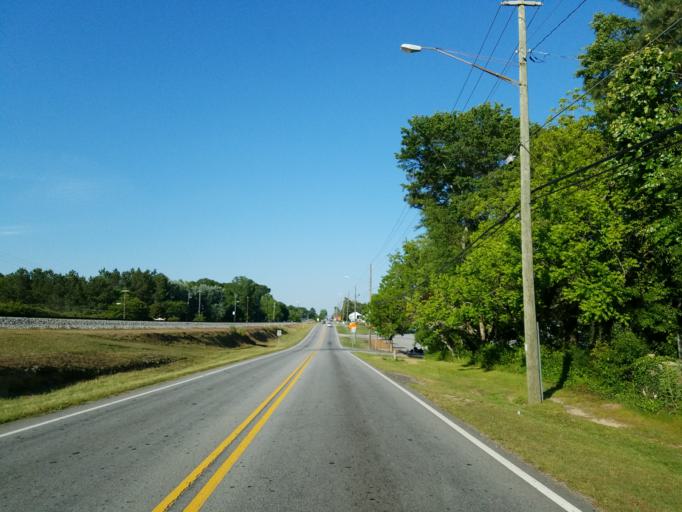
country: US
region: Georgia
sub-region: Douglas County
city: Douglasville
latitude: 33.7461
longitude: -84.7614
